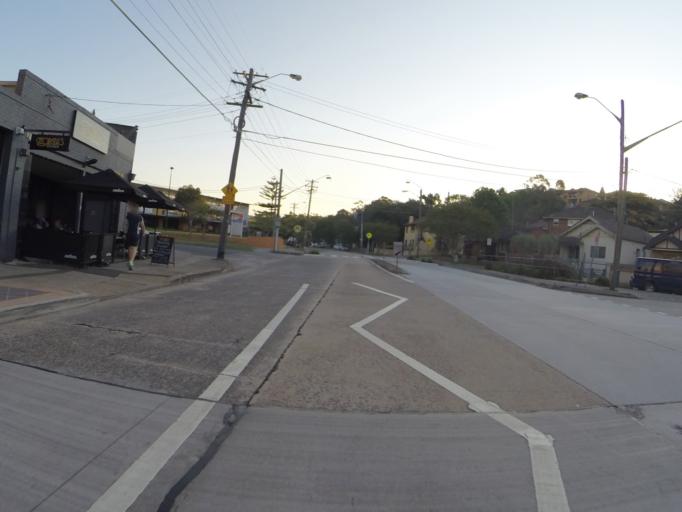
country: AU
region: New South Wales
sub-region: Marrickville
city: Dulwich Hill
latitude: -33.9188
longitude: 151.1460
